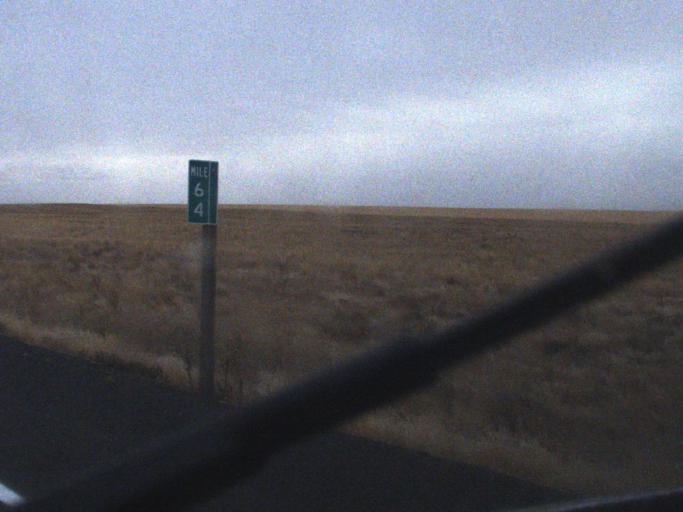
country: US
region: Washington
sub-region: Franklin County
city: Connell
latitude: 46.7944
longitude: -118.6859
